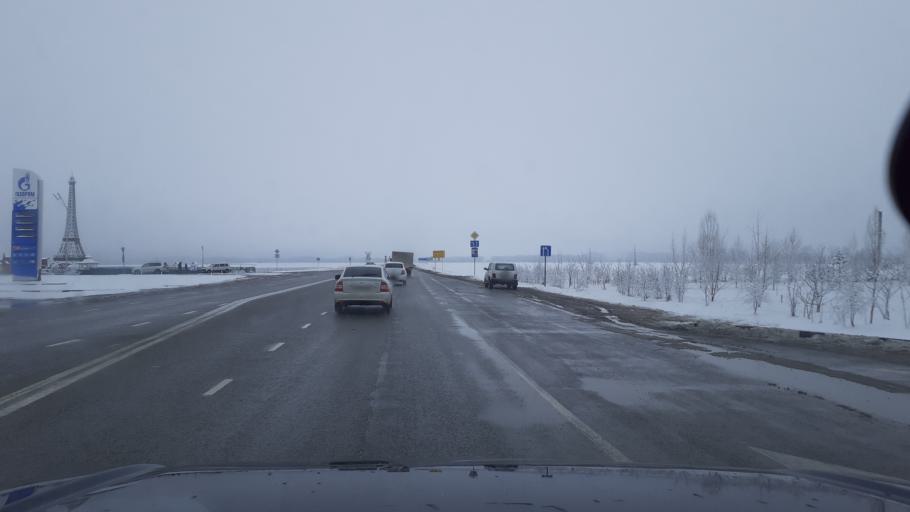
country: RU
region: Adygeya
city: Tul'skiy
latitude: 44.4935
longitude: 40.1650
